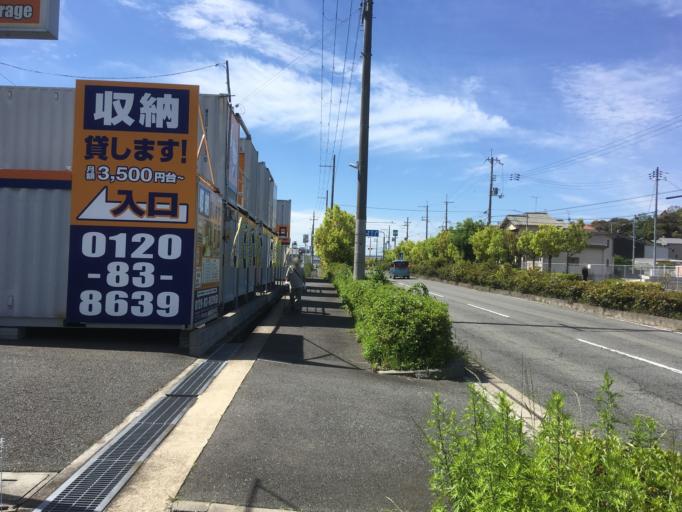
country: JP
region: Nara
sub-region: Ikoma-shi
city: Ikoma
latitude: 34.6760
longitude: 135.7065
